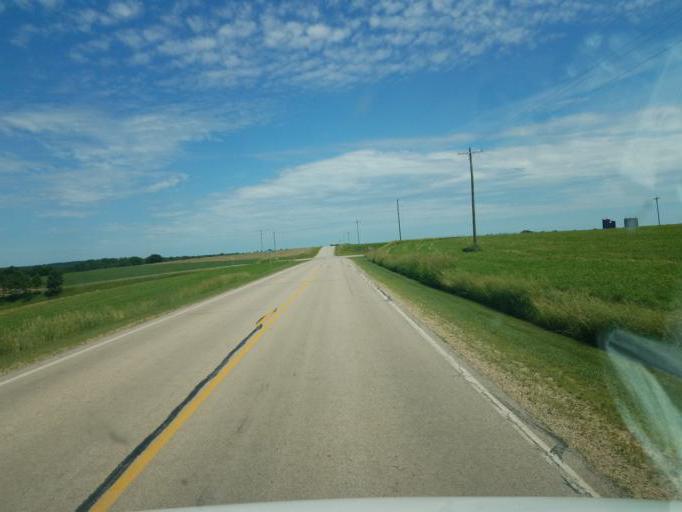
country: US
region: Wisconsin
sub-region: Vernon County
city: Hillsboro
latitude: 43.5974
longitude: -90.2685
